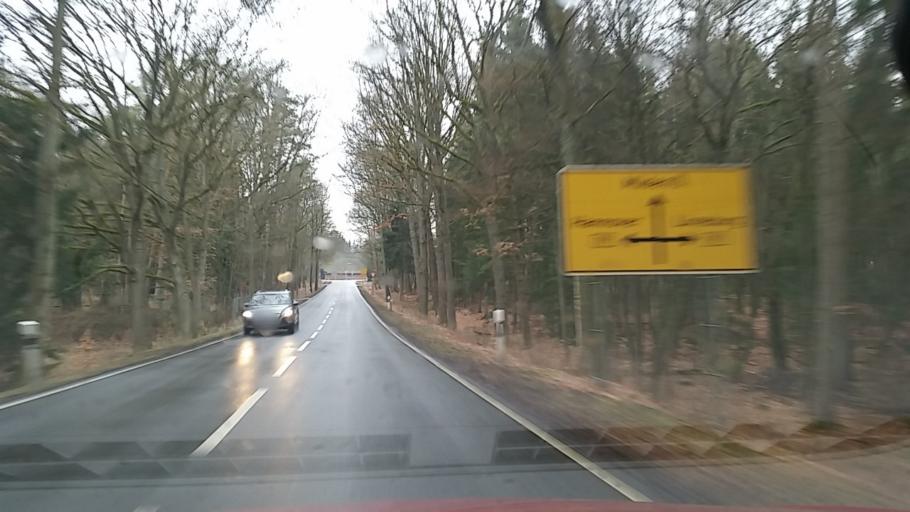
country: DE
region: Lower Saxony
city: Unterluss
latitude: 52.7902
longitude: 10.3870
